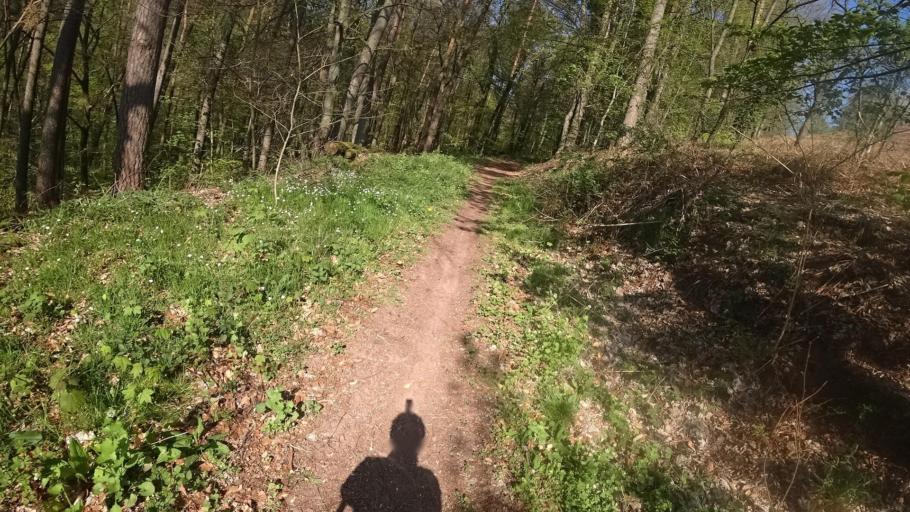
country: DE
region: Rheinland-Pfalz
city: Wawern
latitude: 49.6560
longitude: 6.5325
